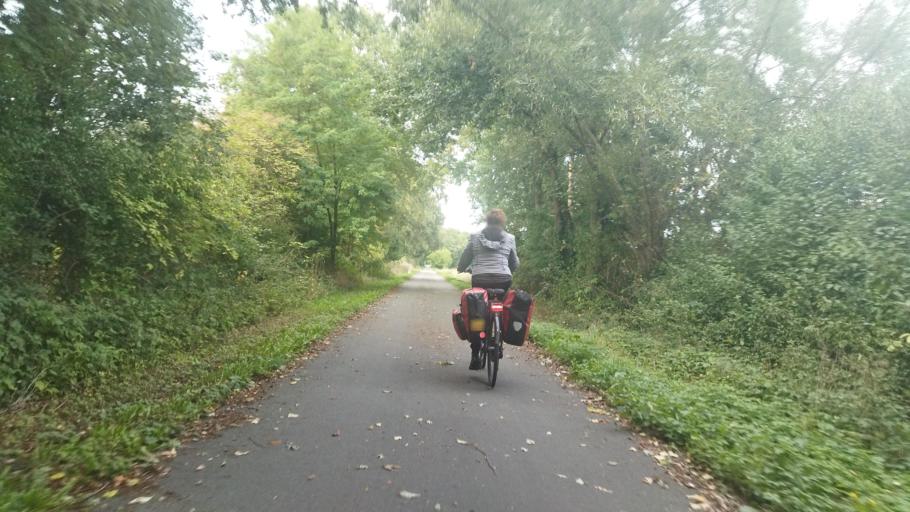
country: DE
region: North Rhine-Westphalia
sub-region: Regierungsbezirk Munster
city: Billerbeck
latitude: 51.9873
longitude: 7.2326
